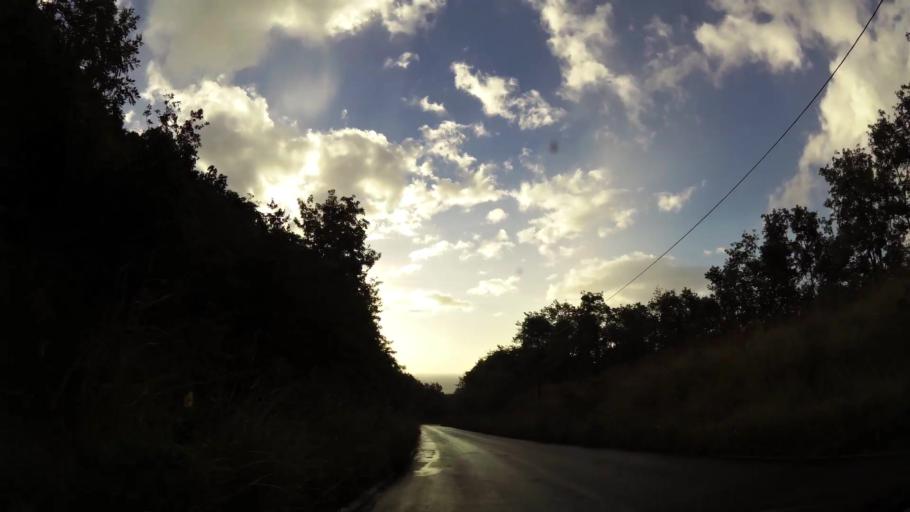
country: DM
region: Saint Peter
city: Colihaut
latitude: 15.5301
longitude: -61.4700
